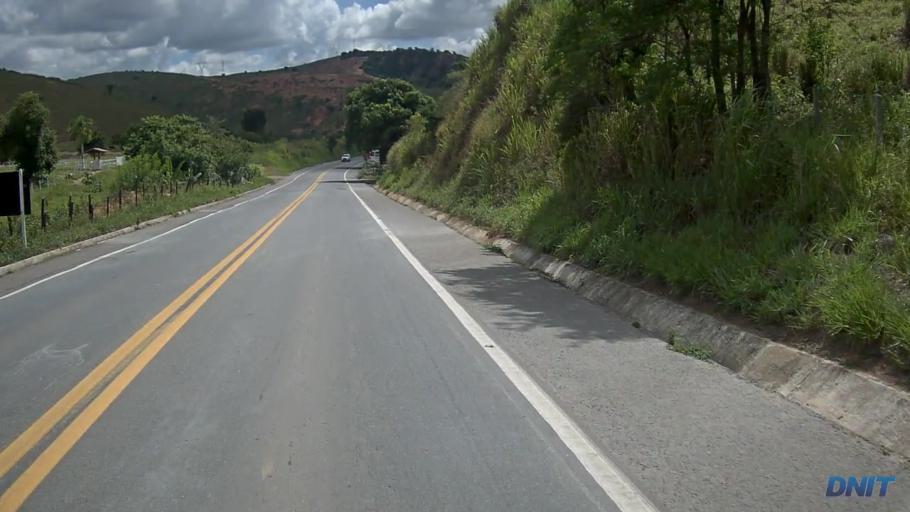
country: BR
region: Minas Gerais
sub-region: Governador Valadares
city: Governador Valadares
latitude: -18.9501
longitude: -42.0704
